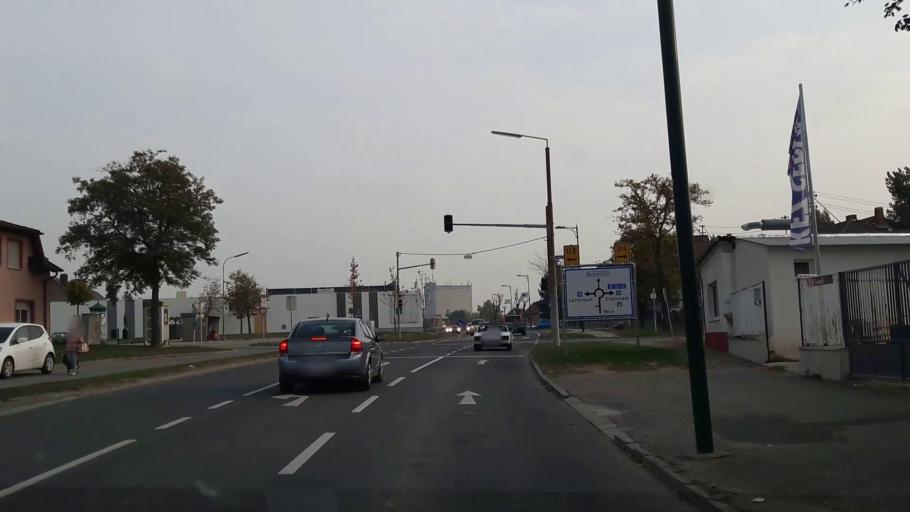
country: AT
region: Burgenland
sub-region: Politischer Bezirk Neusiedl am See
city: Parndorf
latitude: 47.9947
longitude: 16.8563
